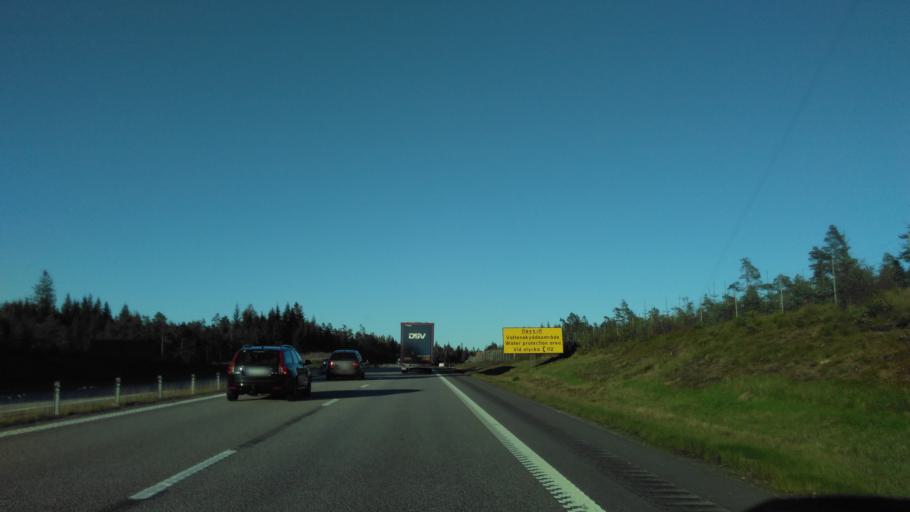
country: SE
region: Vaestra Goetaland
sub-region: Boras Kommun
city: Dalsjofors
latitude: 57.7478
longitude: 13.0696
